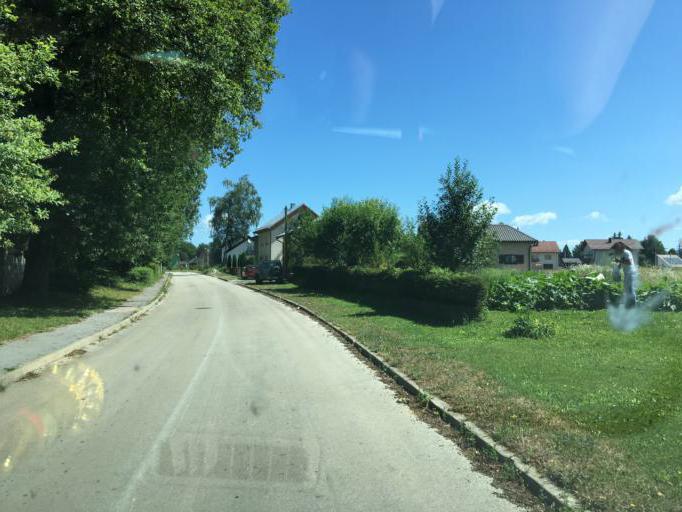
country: HR
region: Licko-Senjska
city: Gospic
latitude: 44.5443
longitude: 15.3568
